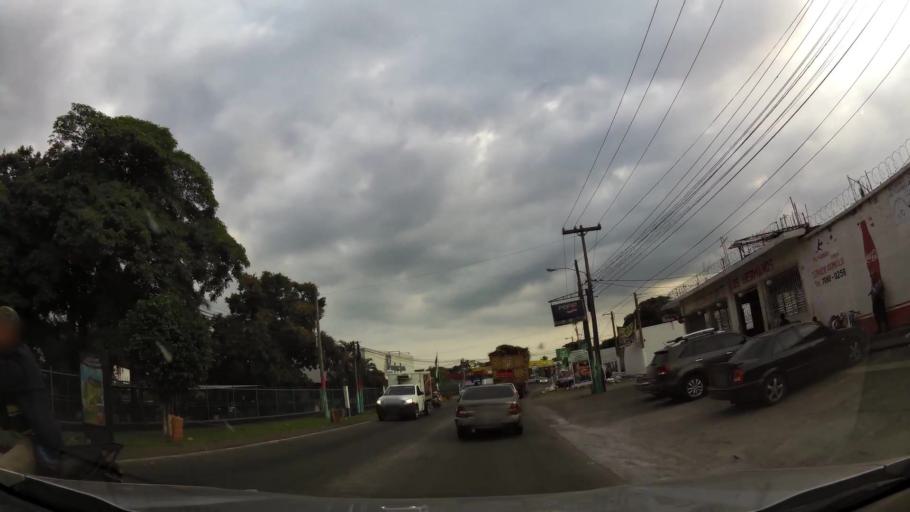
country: GT
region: Escuintla
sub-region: Municipio de Escuintla
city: Escuintla
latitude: 14.3027
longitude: -90.7811
